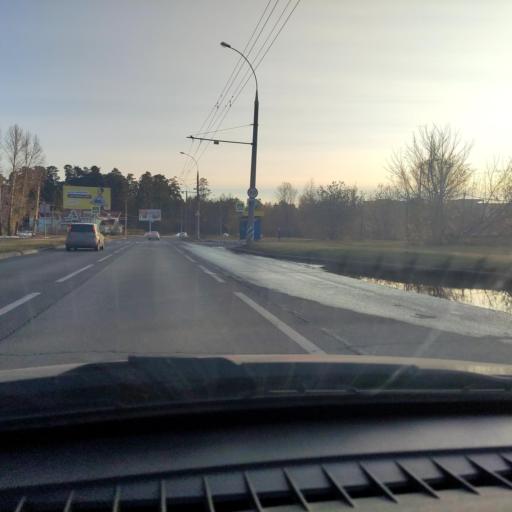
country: RU
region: Samara
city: Tol'yatti
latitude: 53.5002
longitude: 49.2985
